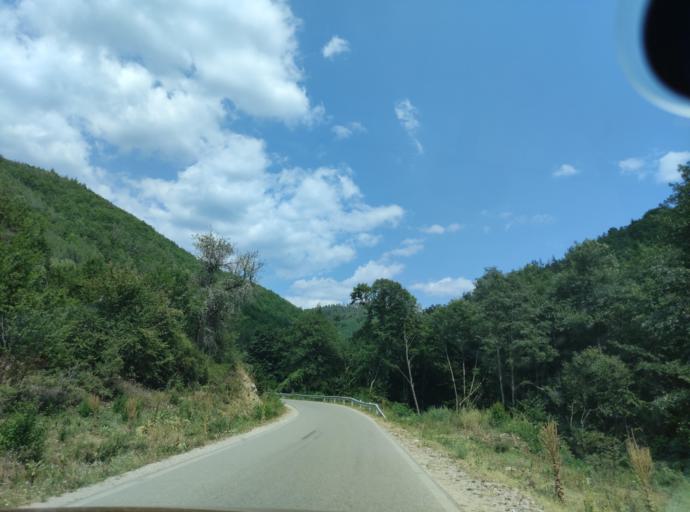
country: BG
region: Blagoevgrad
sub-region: Obshtina Belitsa
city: Belitsa
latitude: 42.0023
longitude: 23.5509
